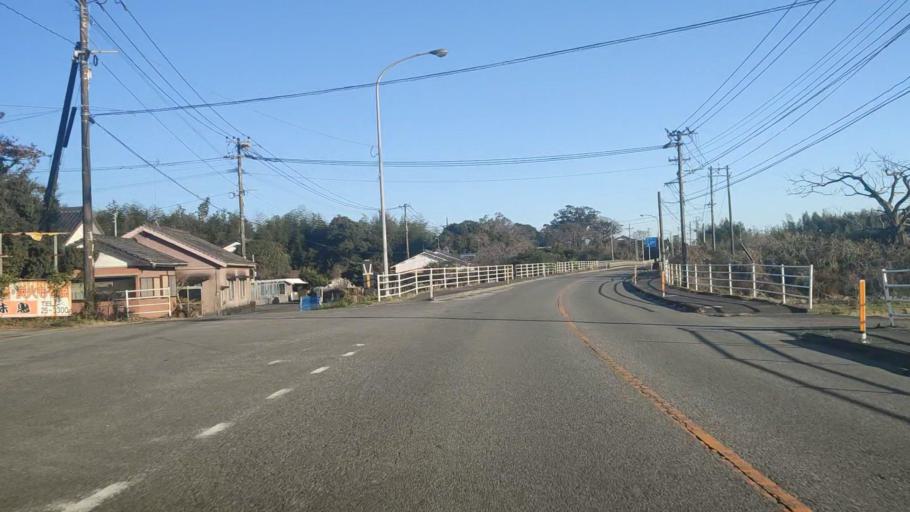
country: JP
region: Miyazaki
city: Takanabe
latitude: 32.2395
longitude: 131.5483
